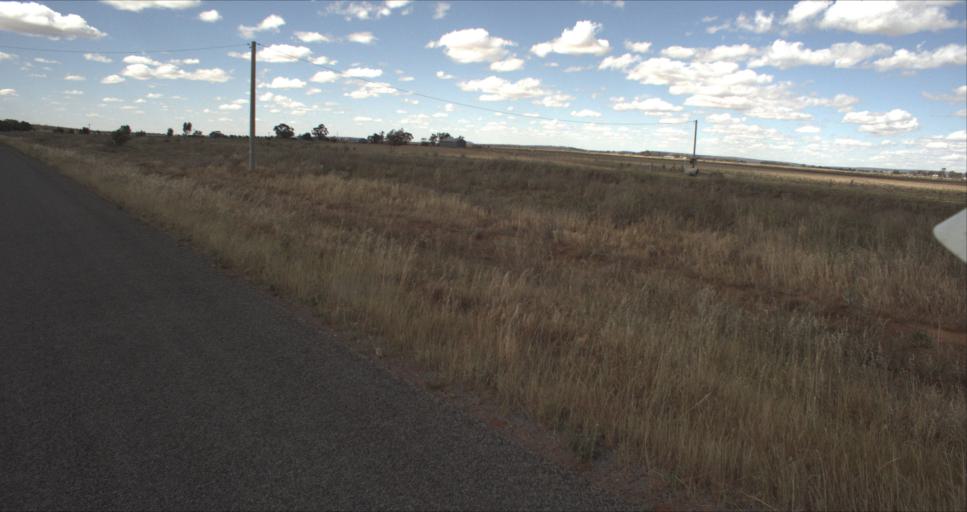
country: AU
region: New South Wales
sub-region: Leeton
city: Leeton
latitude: -34.4502
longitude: 146.2546
